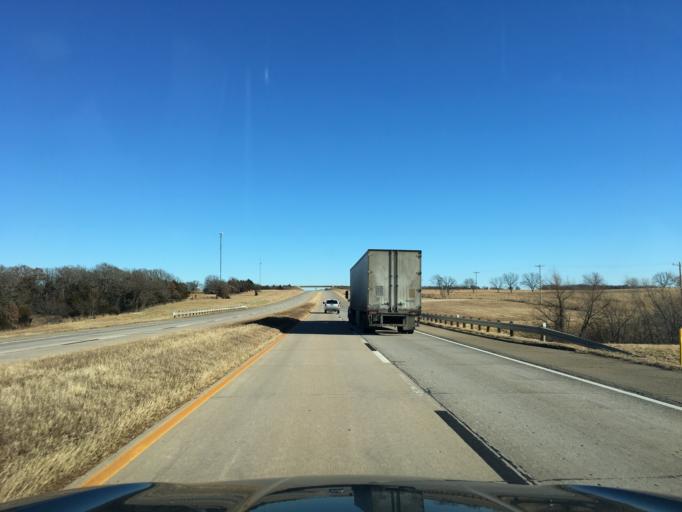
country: US
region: Oklahoma
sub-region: Pawnee County
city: Pawnee
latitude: 36.2244
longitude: -96.7579
